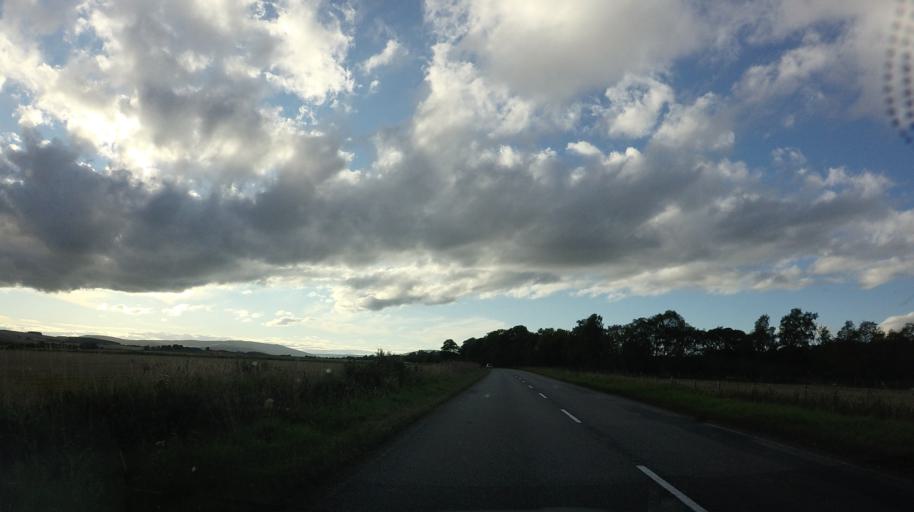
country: GB
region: Scotland
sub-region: Aberdeenshire
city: Alford
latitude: 57.2292
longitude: -2.6524
